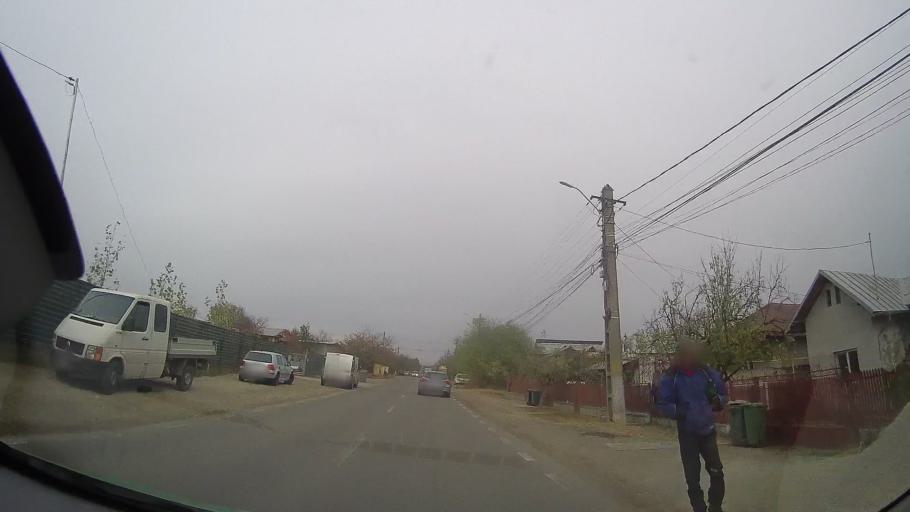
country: RO
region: Prahova
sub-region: Oras Baicoi
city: Liliesti
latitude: 45.0260
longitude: 25.8864
